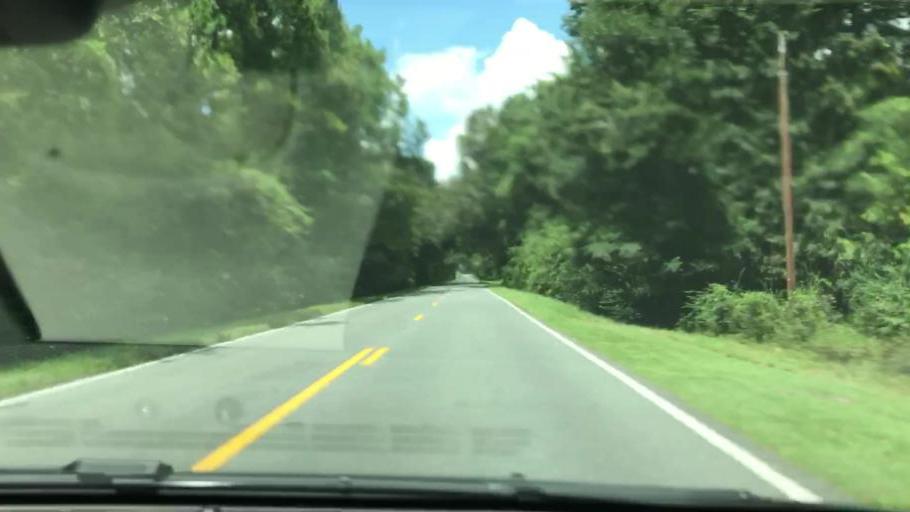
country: US
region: Florida
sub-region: Jackson County
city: Malone
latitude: 30.9447
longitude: -85.1183
